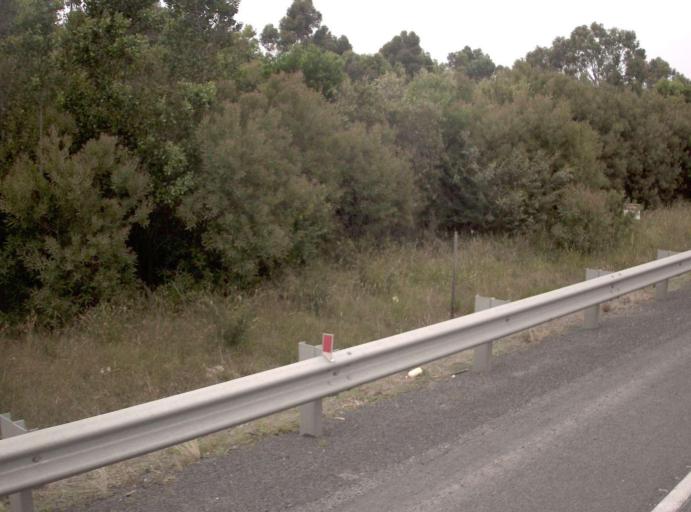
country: AU
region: Victoria
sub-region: Latrobe
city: Morwell
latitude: -38.2248
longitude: 146.4660
